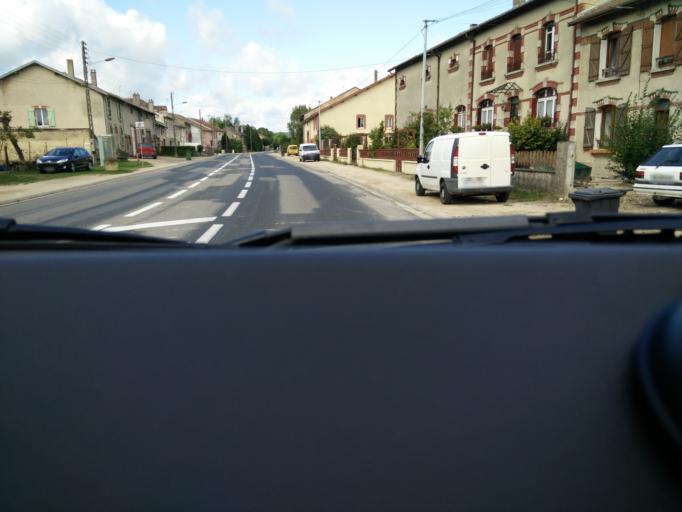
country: FR
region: Lorraine
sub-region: Departement de la Meuse
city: Etain
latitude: 49.1111
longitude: 5.5964
